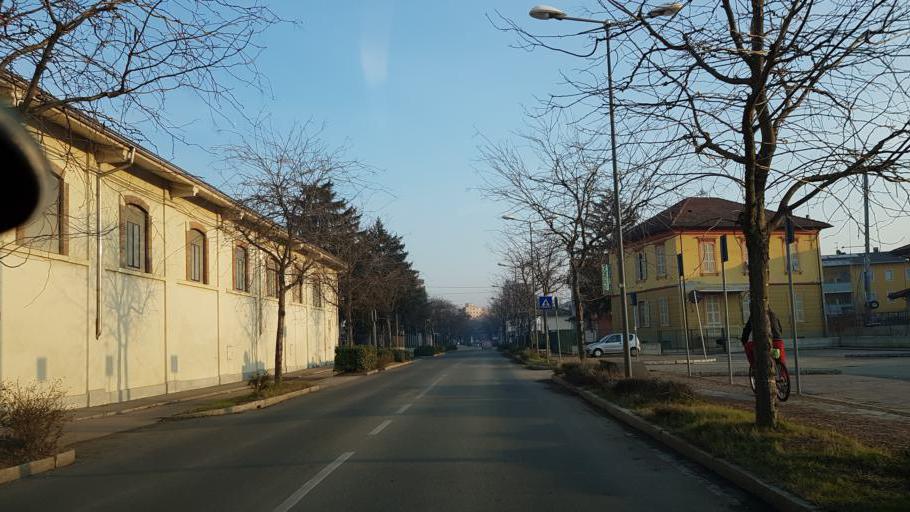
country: IT
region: Piedmont
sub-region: Provincia di Alessandria
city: Novi Ligure
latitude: 44.7660
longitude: 8.7788
